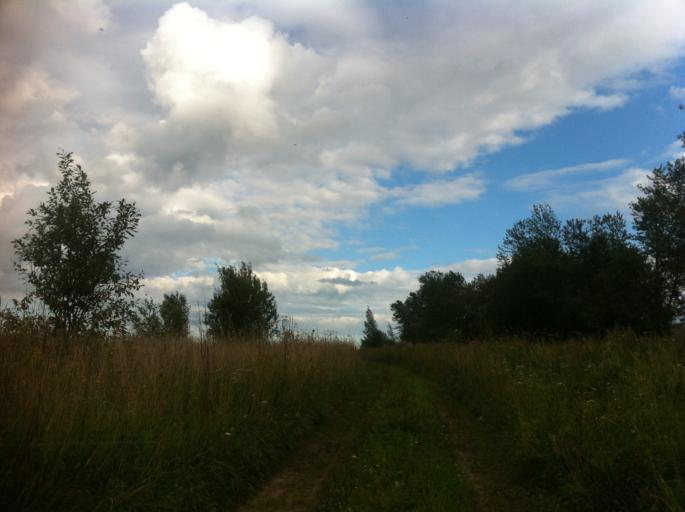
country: RU
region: Pskov
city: Izborsk
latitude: 57.8187
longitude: 27.9740
